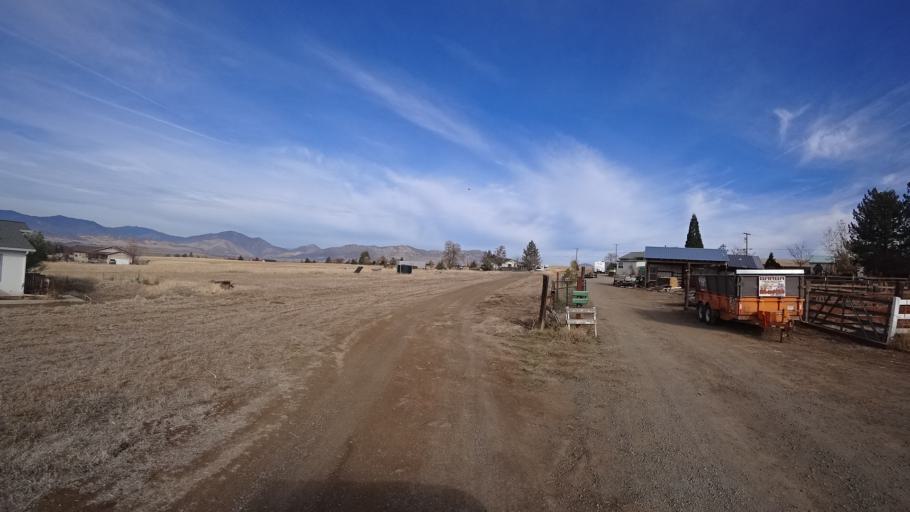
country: US
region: California
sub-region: Siskiyou County
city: Montague
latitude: 41.7293
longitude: -122.5154
